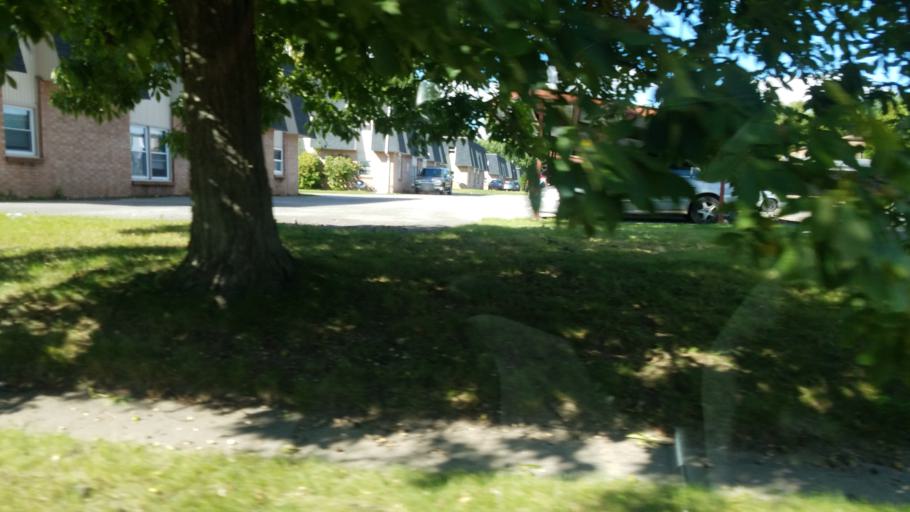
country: US
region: Ohio
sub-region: Mahoning County
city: Boardman
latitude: 41.0465
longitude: -80.6679
